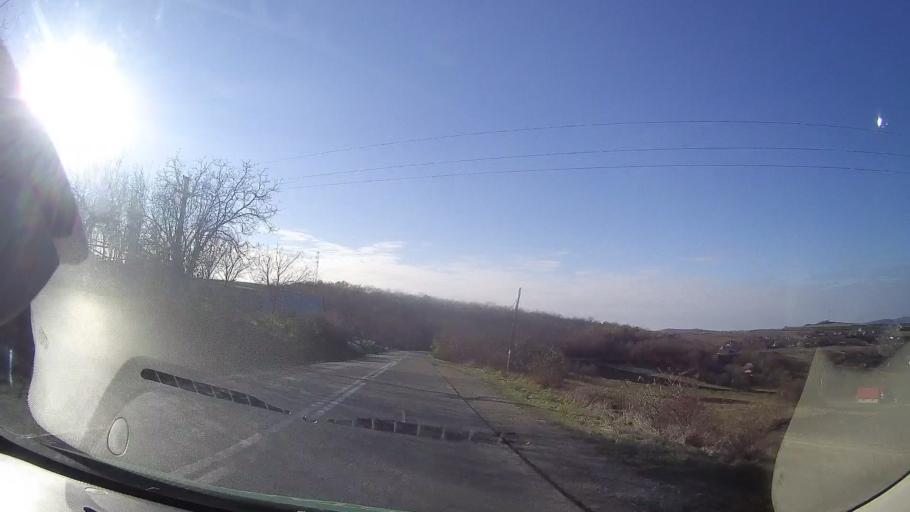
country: RO
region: Cluj
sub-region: Comuna Mociu
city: Mociu
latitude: 46.7924
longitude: 24.0675
